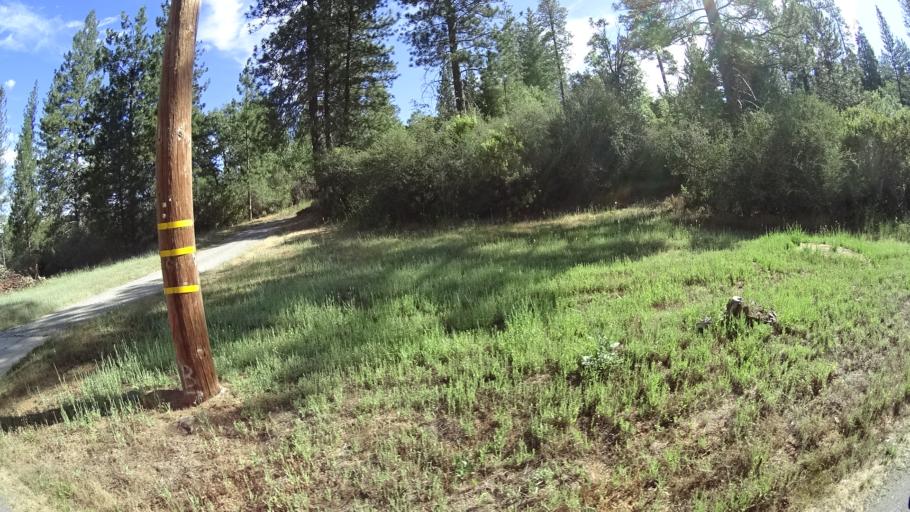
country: US
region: California
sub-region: Amador County
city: Pioneer
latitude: 38.3729
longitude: -120.4622
